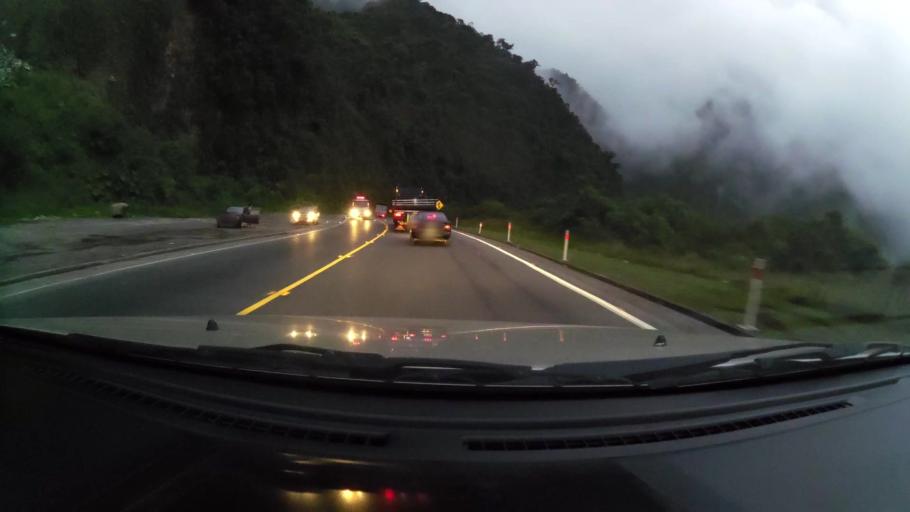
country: EC
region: Pichincha
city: Machachi
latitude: -0.4475
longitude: -78.6841
